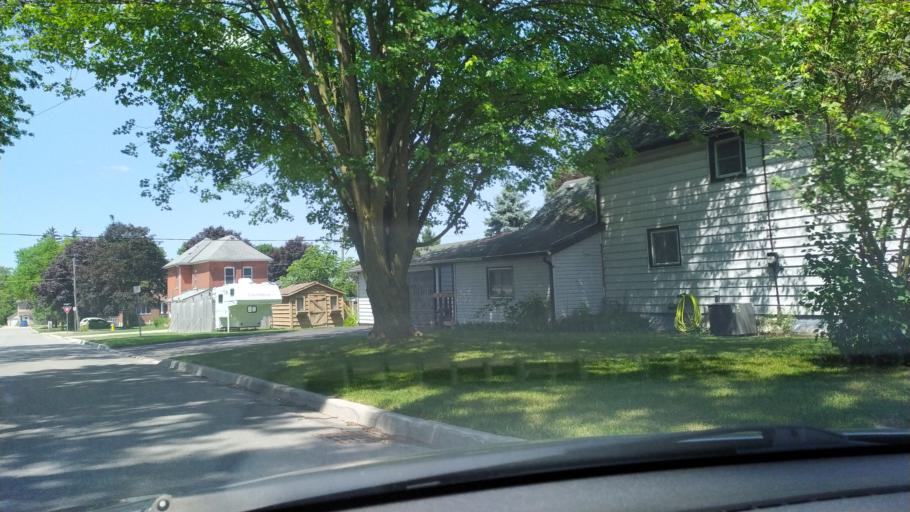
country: CA
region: Ontario
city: Stratford
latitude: 43.3597
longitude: -80.9868
